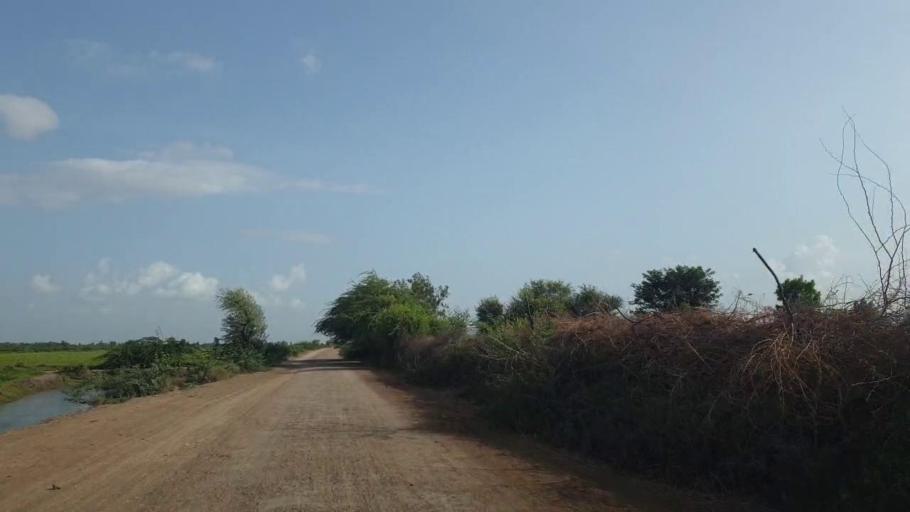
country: PK
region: Sindh
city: Kadhan
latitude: 24.6373
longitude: 69.0960
